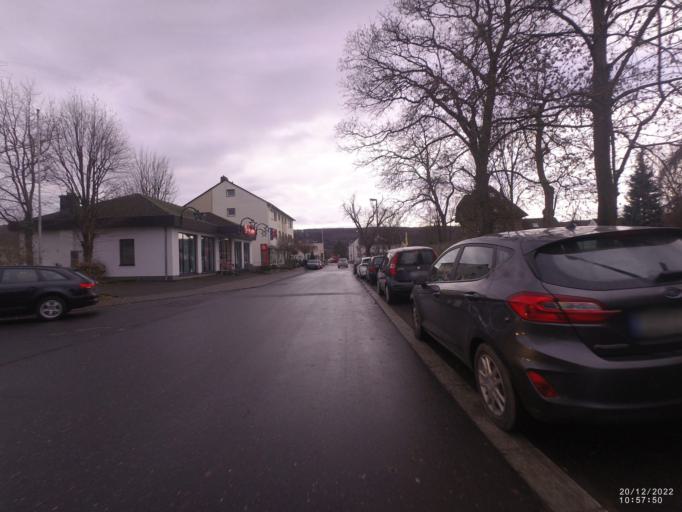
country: DE
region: Rheinland-Pfalz
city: Remagen
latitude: 50.5572
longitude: 7.2176
